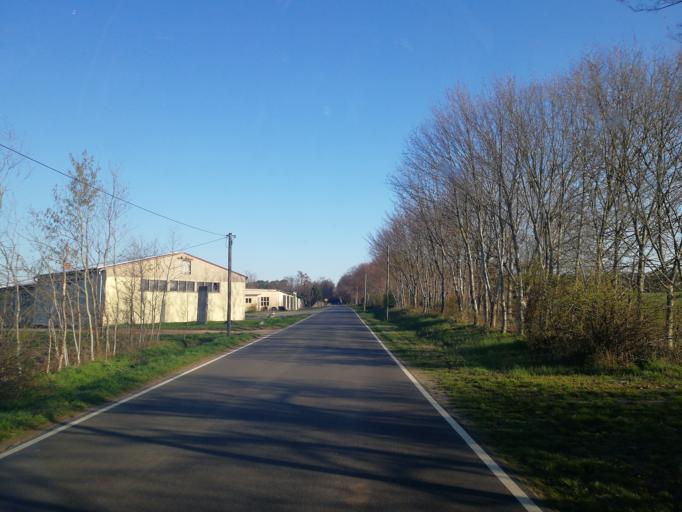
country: DE
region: Brandenburg
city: Drahnsdorf
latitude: 51.8951
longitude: 13.6082
